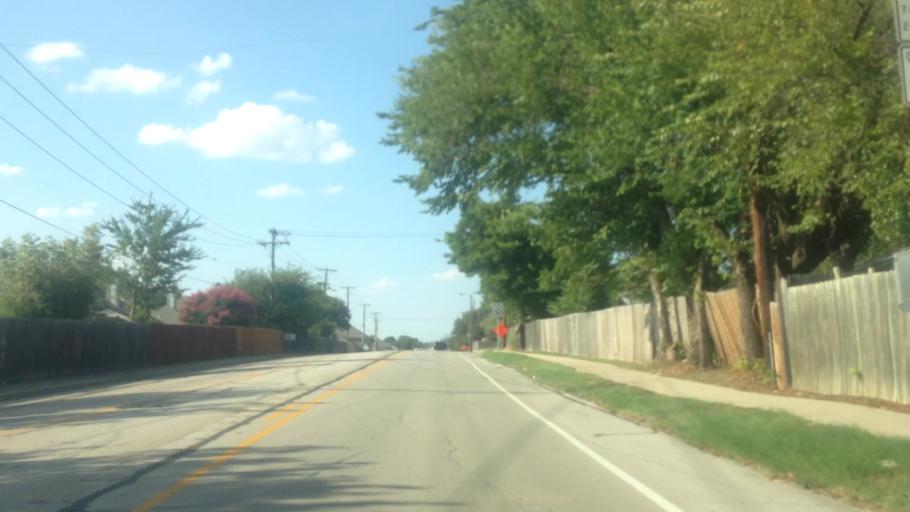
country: US
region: Texas
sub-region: Tarrant County
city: Watauga
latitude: 32.8780
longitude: -97.2550
